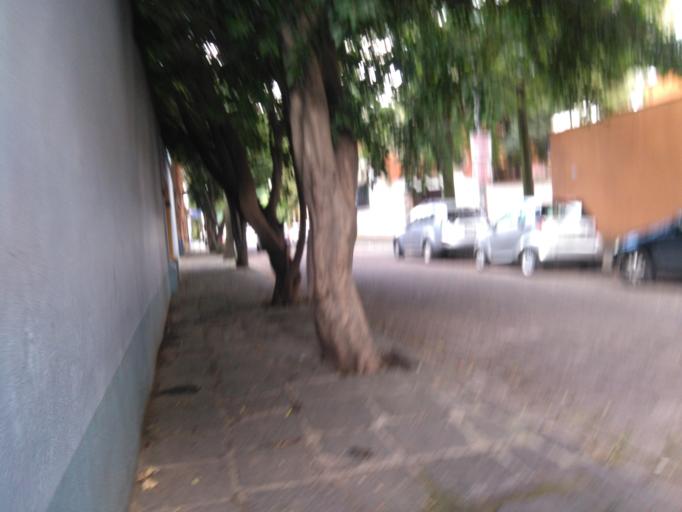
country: MX
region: Mexico City
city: Coyoacan
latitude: 19.3494
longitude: -99.1721
